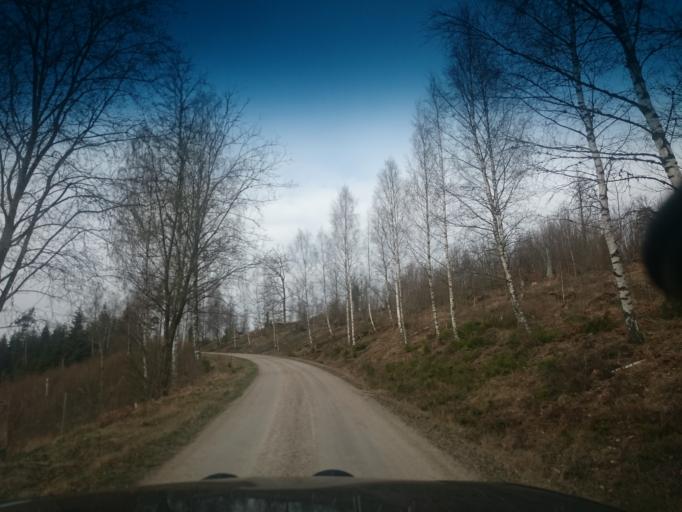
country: SE
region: Joenkoeping
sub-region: Vetlanda Kommun
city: Vetlanda
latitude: 57.3290
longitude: 15.1590
